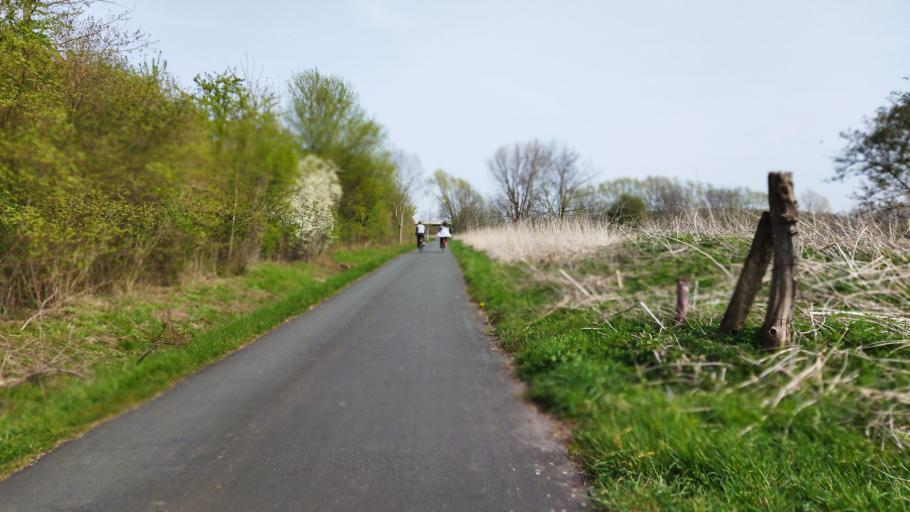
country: DE
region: North Rhine-Westphalia
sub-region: Regierungsbezirk Detmold
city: Minden
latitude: 52.2672
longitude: 8.9236
